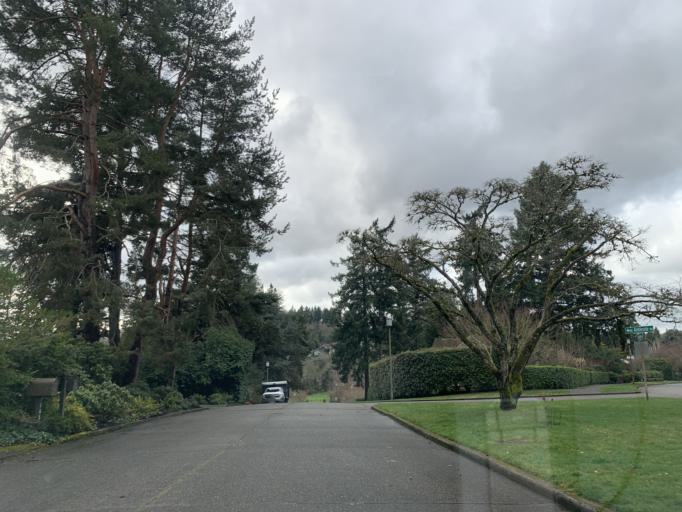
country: US
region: Washington
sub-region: King County
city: Yarrow Point
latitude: 47.6668
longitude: -122.2637
